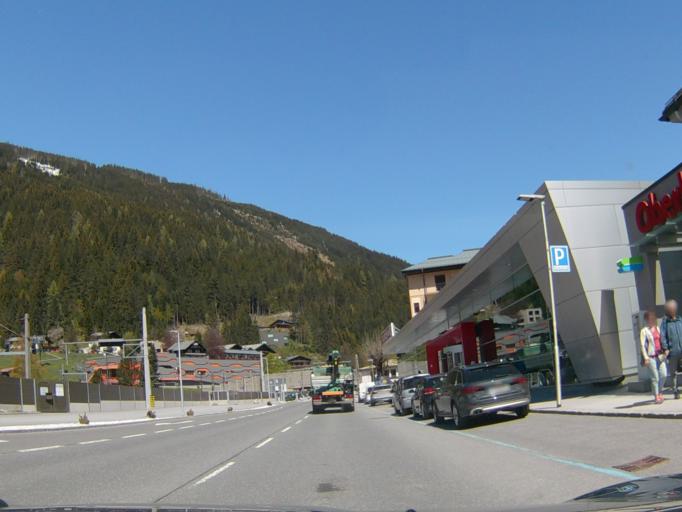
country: AT
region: Salzburg
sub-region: Politischer Bezirk Sankt Johann im Pongau
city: Bad Gastein
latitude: 47.1094
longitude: 13.1337
